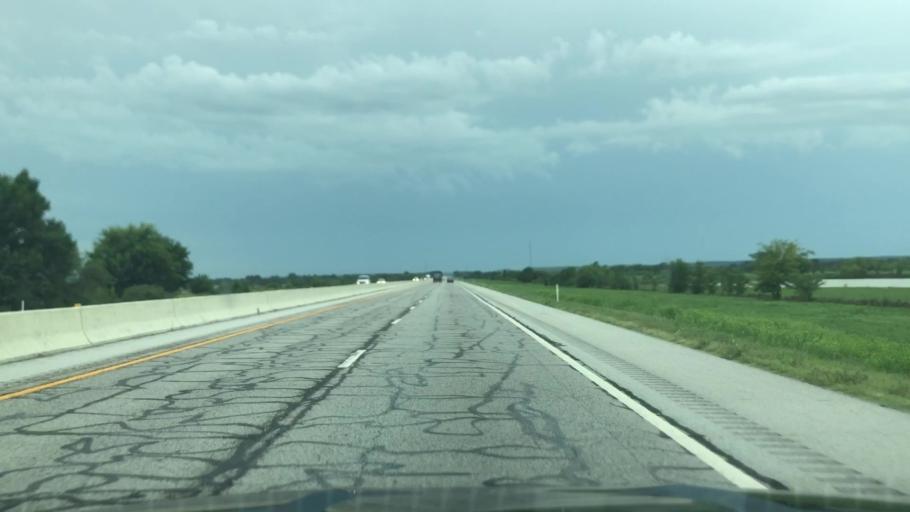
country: US
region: Oklahoma
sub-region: Craig County
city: Vinita
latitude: 36.5230
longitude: -95.2564
